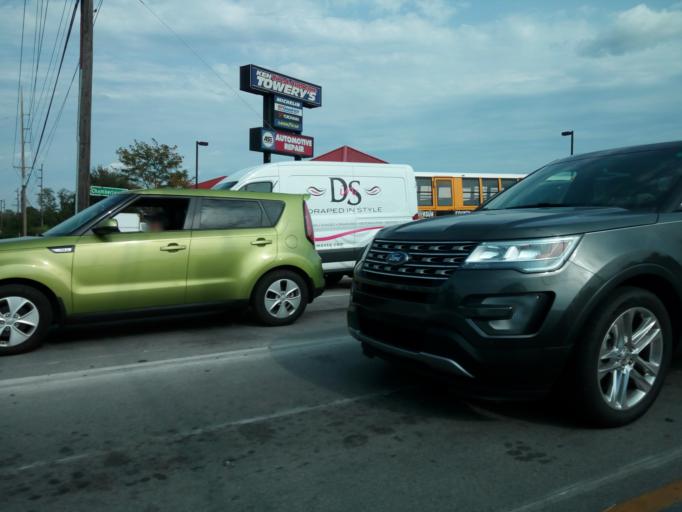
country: US
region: Kentucky
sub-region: Jefferson County
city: Worthington Hills
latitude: 38.2991
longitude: -85.5416
